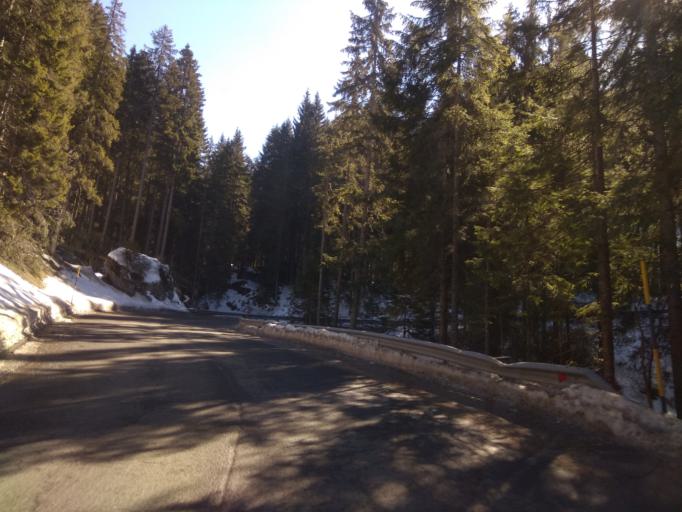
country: IT
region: Trentino-Alto Adige
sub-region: Bolzano
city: Nova Levante
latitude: 46.4153
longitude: 11.5669
